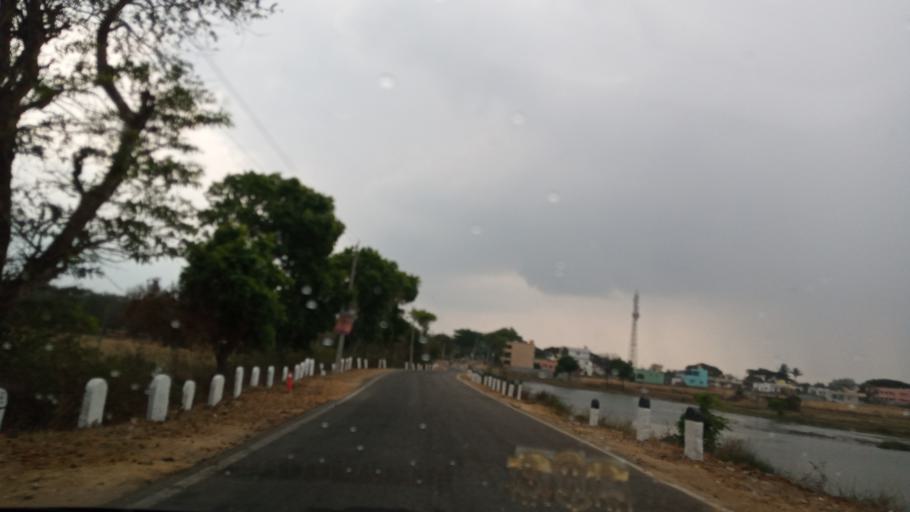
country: IN
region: Karnataka
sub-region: Kolar
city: Mulbagal
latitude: 13.1115
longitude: 78.3354
